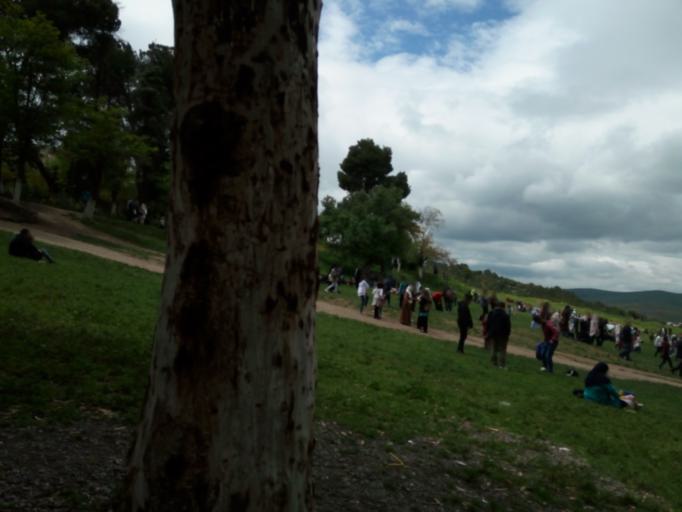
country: DZ
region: Setif
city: El Eulma
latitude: 36.3174
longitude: 5.7374
